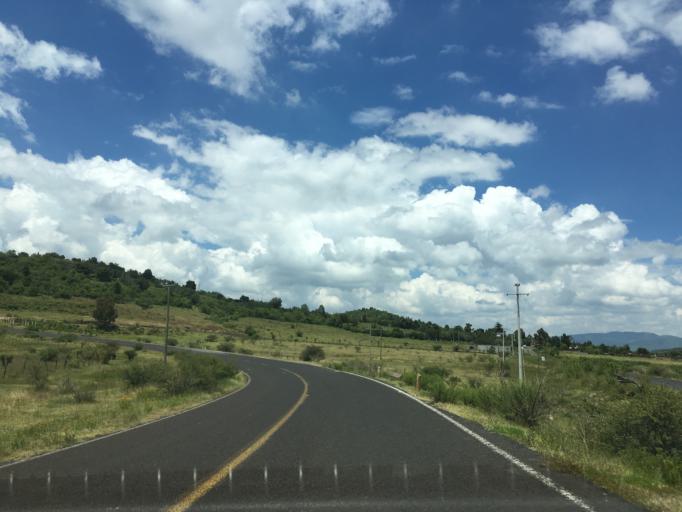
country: MX
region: Mexico
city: Huaniqueo de Morales
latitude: 19.8017
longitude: -101.4477
